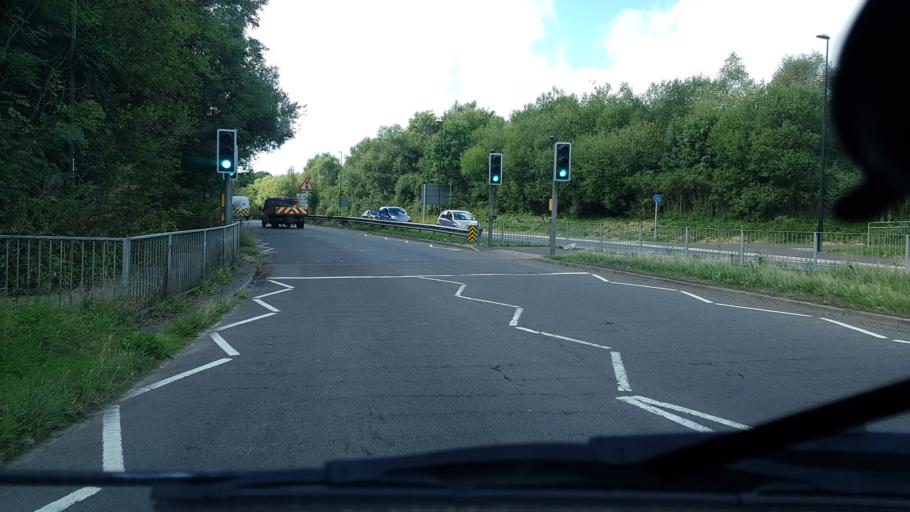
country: GB
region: England
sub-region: West Sussex
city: Broadfield
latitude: 51.0868
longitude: -0.1989
